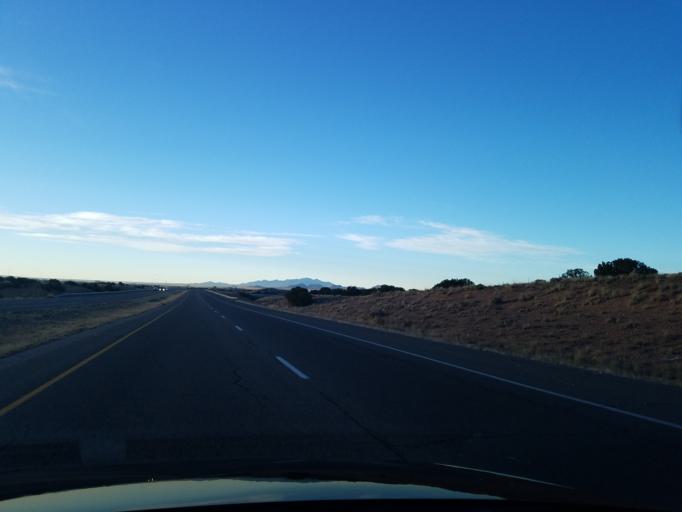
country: US
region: New Mexico
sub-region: Santa Fe County
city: Agua Fria
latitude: 35.6254
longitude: -106.0710
